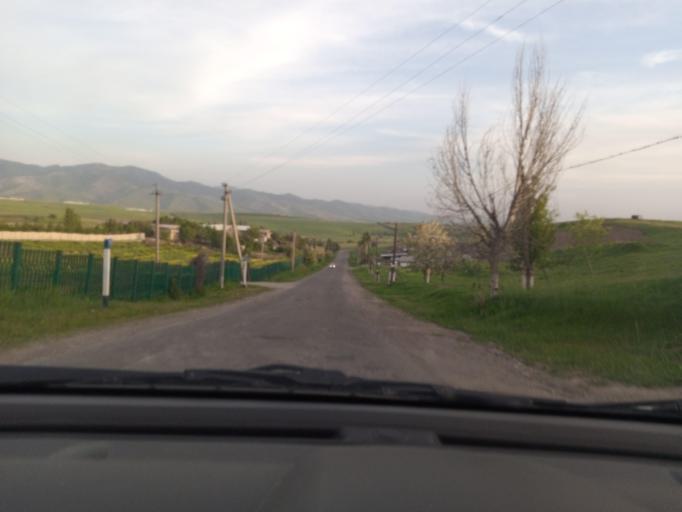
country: UZ
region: Toshkent
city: Parkent
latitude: 41.2345
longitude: 69.7374
